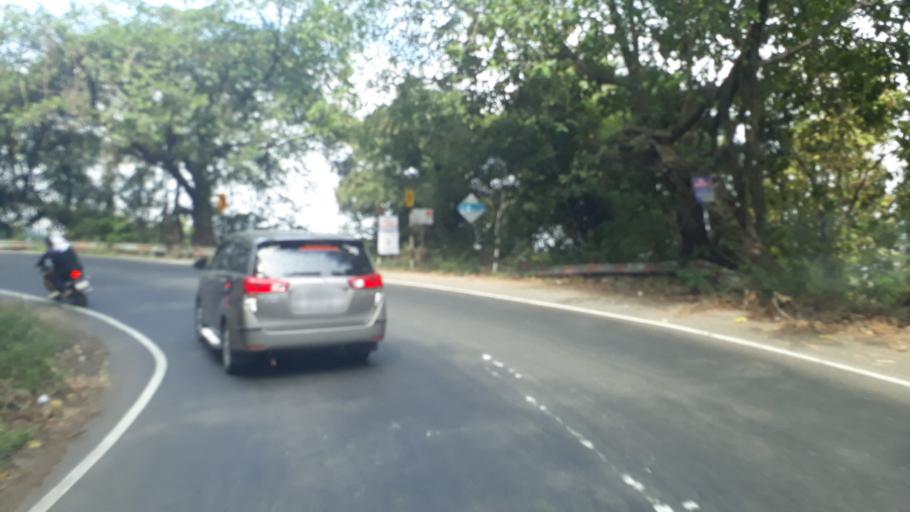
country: IN
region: Maharashtra
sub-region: Raigarh
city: Alibag
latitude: 18.6967
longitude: 72.9299
